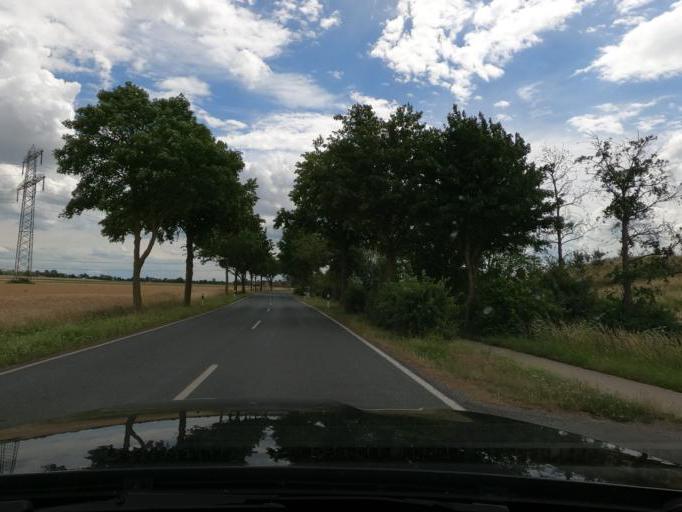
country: DE
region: Lower Saxony
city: Sehnde
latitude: 52.3471
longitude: 9.9011
